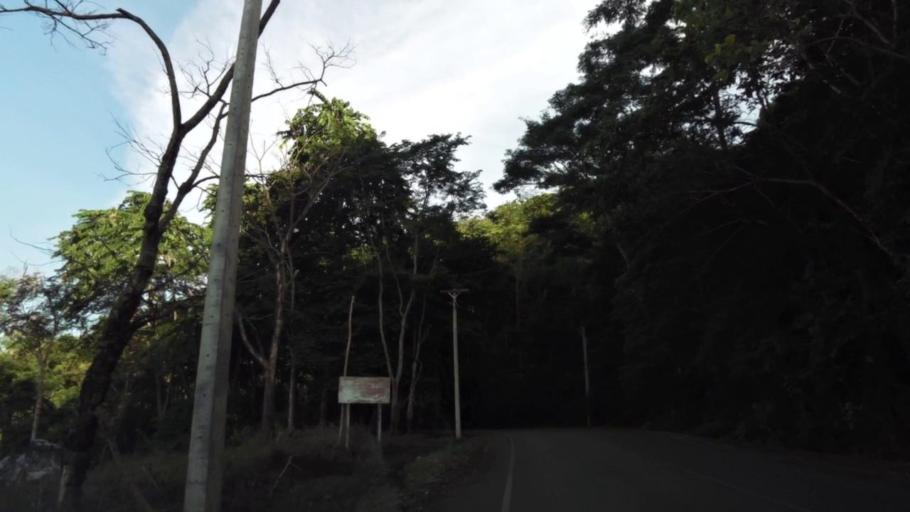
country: TH
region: Chiang Rai
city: Khun Tan
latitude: 19.8648
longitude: 100.4447
